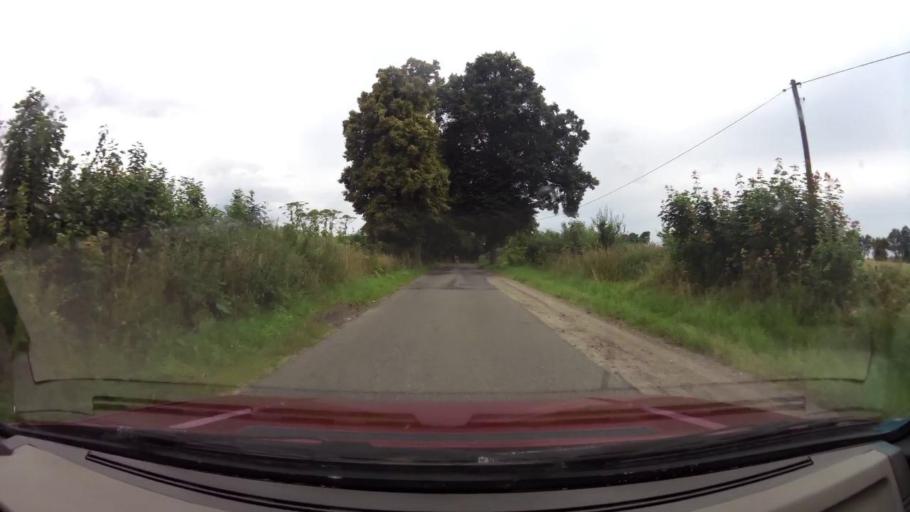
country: PL
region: West Pomeranian Voivodeship
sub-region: Powiat bialogardzki
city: Bialogard
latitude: 53.9510
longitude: 15.9642
